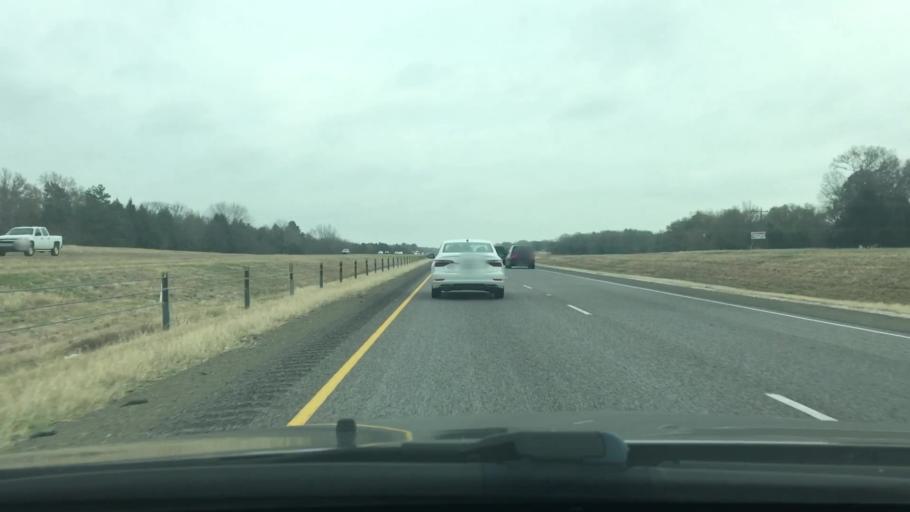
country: US
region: Texas
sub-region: Freestone County
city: Fairfield
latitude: 31.7466
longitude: -96.1964
